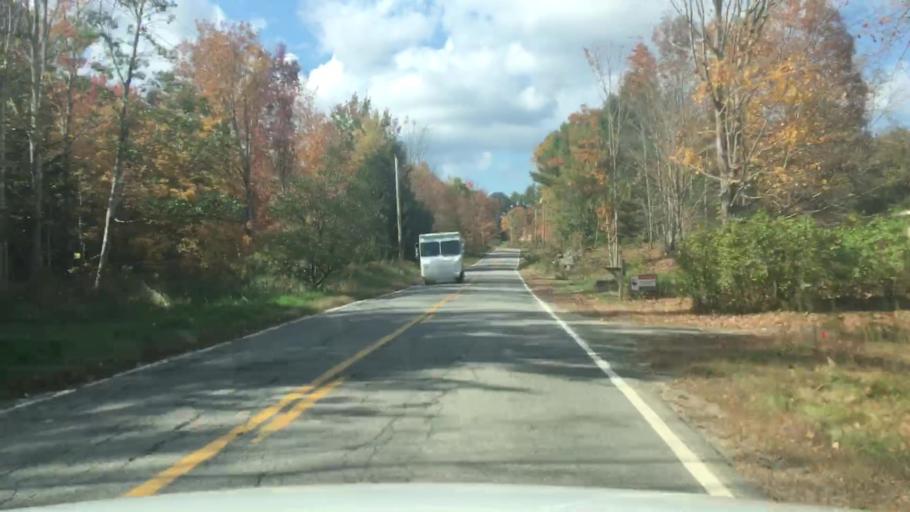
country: US
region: Maine
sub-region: Knox County
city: Washington
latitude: 44.3036
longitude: -69.3322
